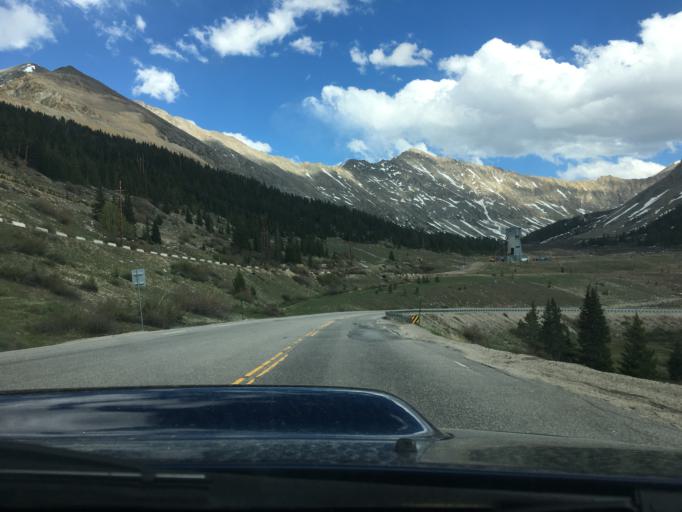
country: US
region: Colorado
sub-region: Lake County
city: Leadville
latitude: 39.3636
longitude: -106.1804
